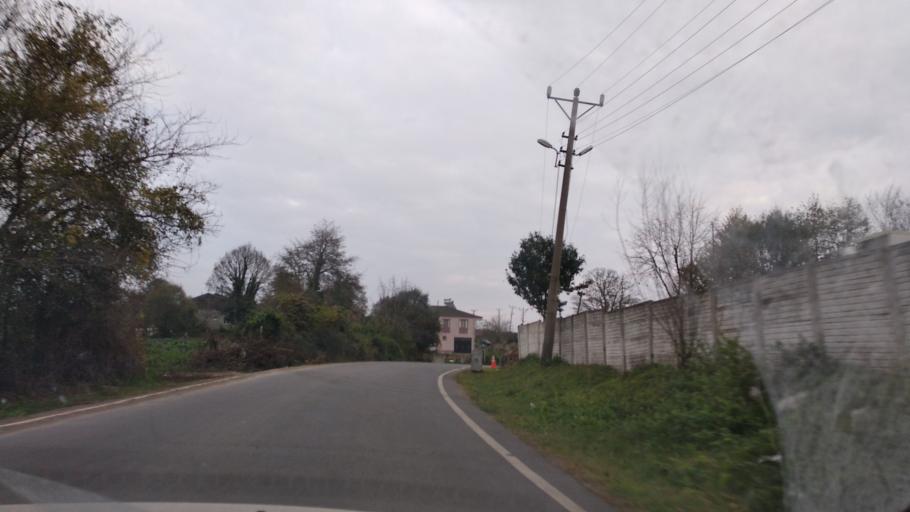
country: TR
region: Sakarya
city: Ortakoy
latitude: 41.0344
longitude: 30.6609
